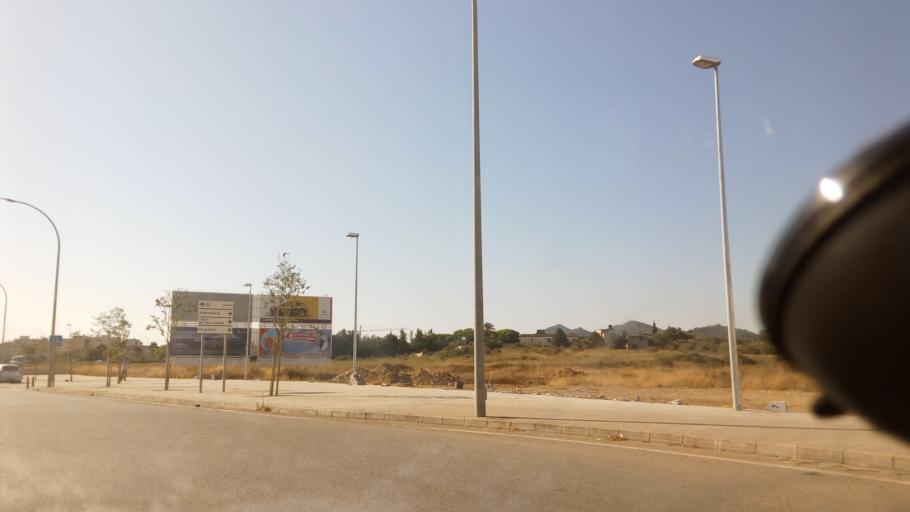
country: ES
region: Balearic Islands
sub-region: Illes Balears
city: Manacor
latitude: 39.5724
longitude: 3.1945
